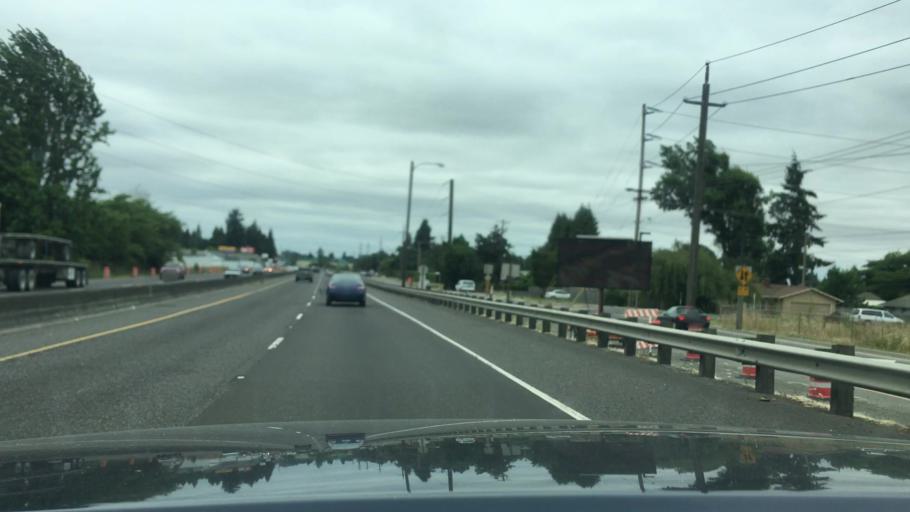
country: US
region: Oregon
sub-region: Lane County
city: Eugene
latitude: 44.0976
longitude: -123.1133
